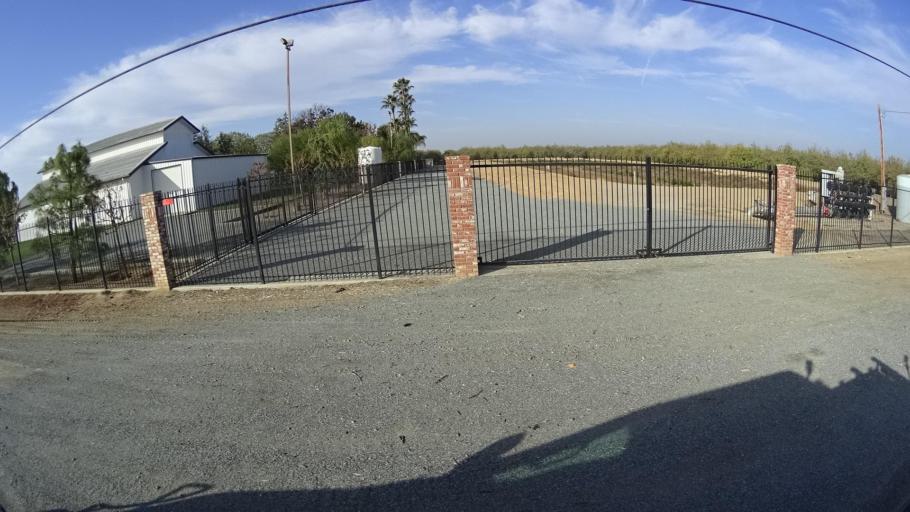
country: US
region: California
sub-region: Kern County
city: McFarland
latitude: 35.6682
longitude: -119.2047
